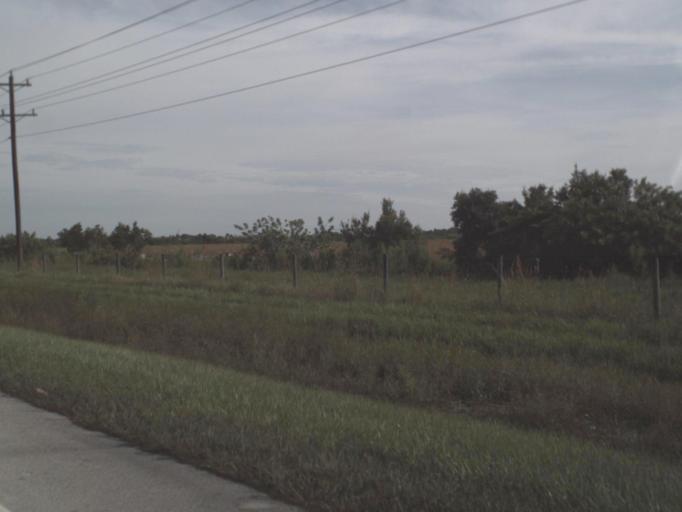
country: US
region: Florida
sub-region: Lee County
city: Fort Myers Shores
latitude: 26.7598
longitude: -81.7608
